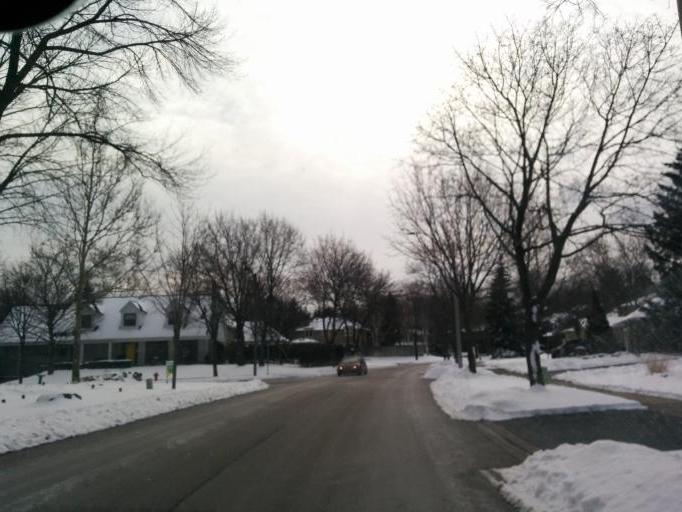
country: CA
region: Ontario
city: Mississauga
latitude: 43.5371
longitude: -79.6580
